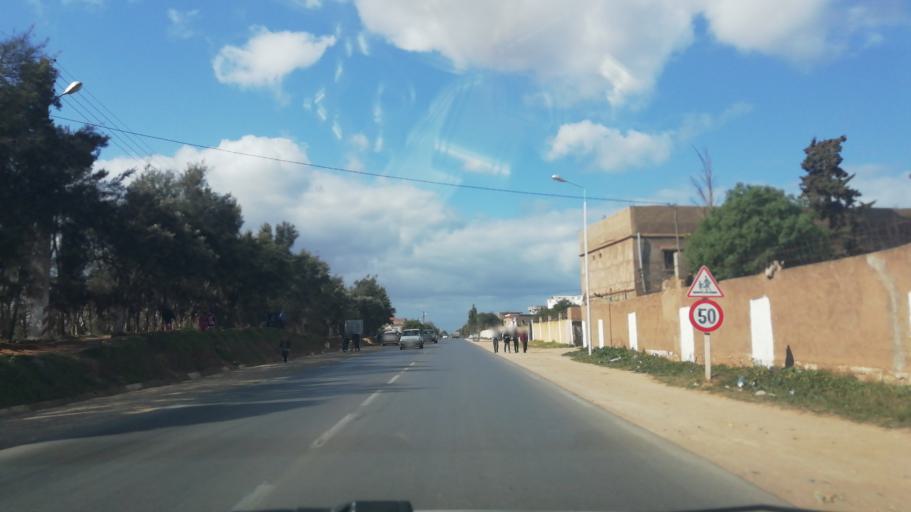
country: DZ
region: Relizane
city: Mazouna
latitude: 36.2593
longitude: 0.6026
